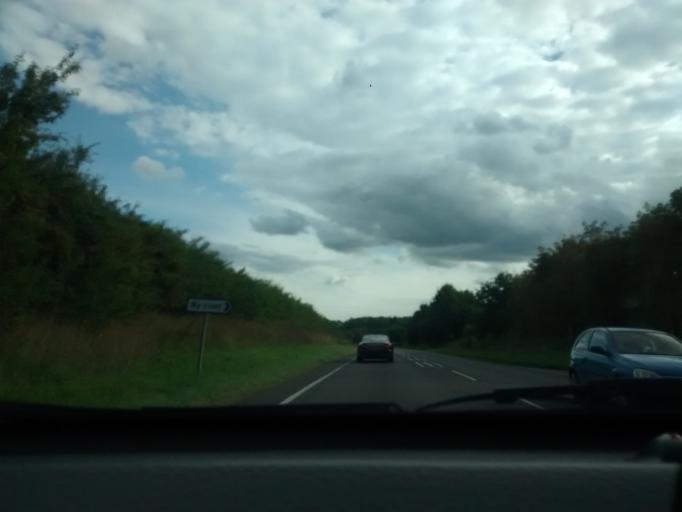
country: GB
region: England
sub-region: Norfolk
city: Downham Market
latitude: 52.5785
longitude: 0.3883
